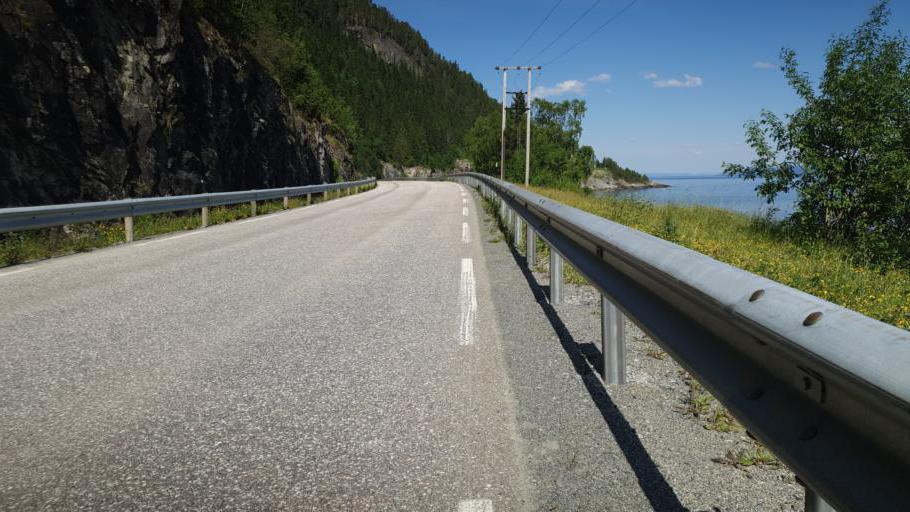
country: NO
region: Nord-Trondelag
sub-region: Leksvik
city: Leksvik
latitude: 63.6067
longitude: 10.4909
